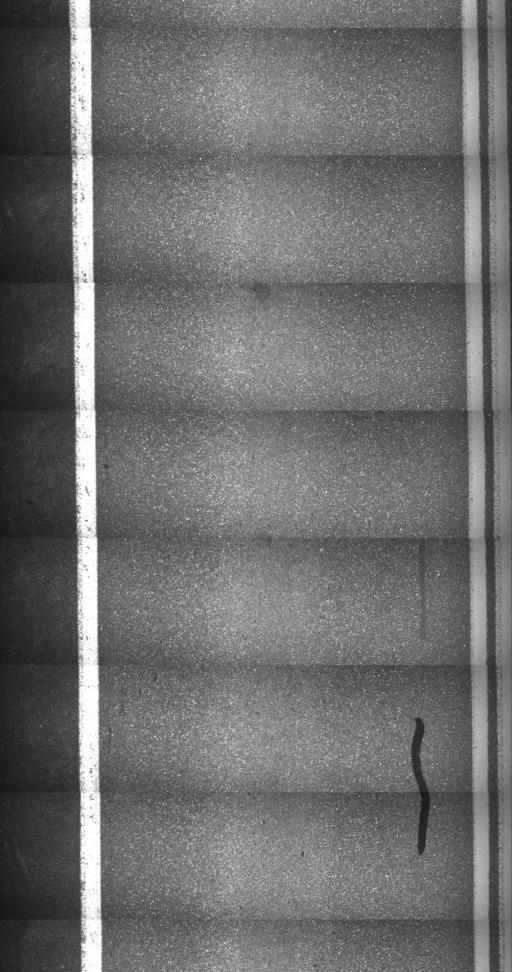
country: US
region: Vermont
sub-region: Windham County
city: Newfane
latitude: 43.0708
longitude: -72.7049
